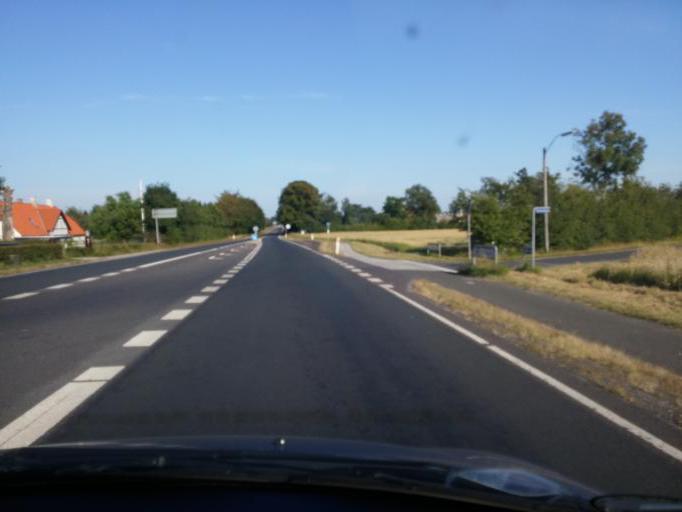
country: DK
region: South Denmark
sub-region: Odense Kommune
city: Neder Holluf
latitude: 55.3898
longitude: 10.4659
